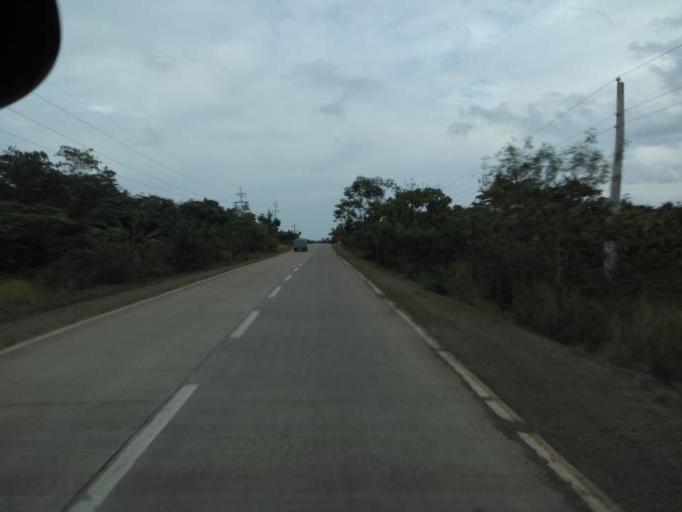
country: PH
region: Cagayan Valley
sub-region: Province of Cagayan
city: Magapit
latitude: 18.1478
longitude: 121.7339
